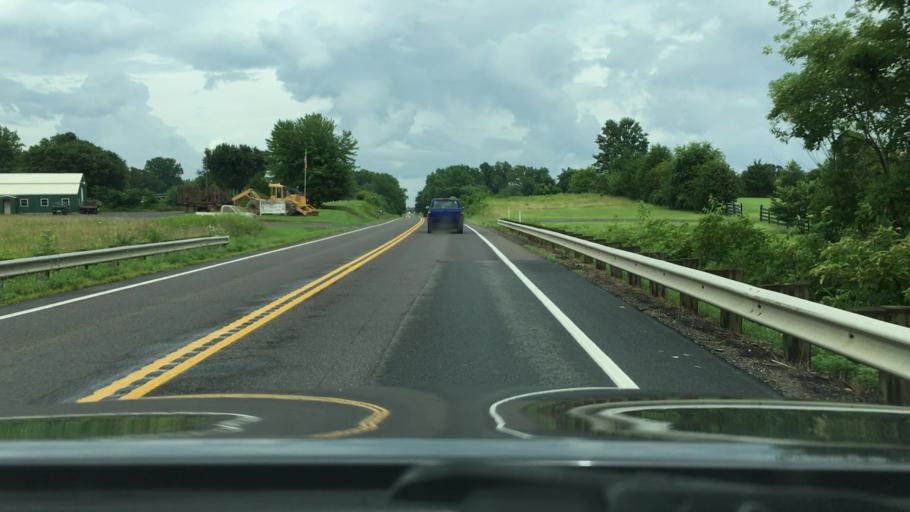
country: US
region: Virginia
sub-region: Orange County
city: Orange
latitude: 38.2625
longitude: -77.9723
